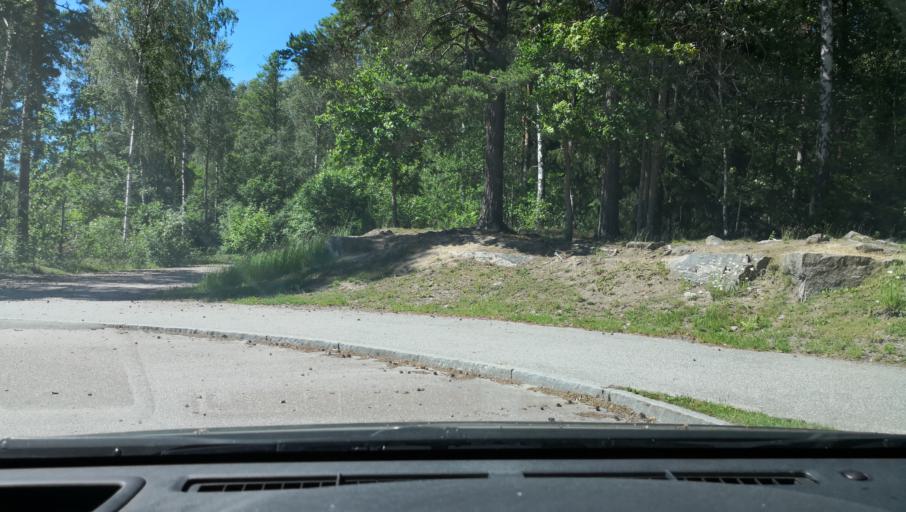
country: SE
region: Vaestmanland
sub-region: Kungsors Kommun
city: Kungsoer
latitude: 59.2823
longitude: 16.1098
